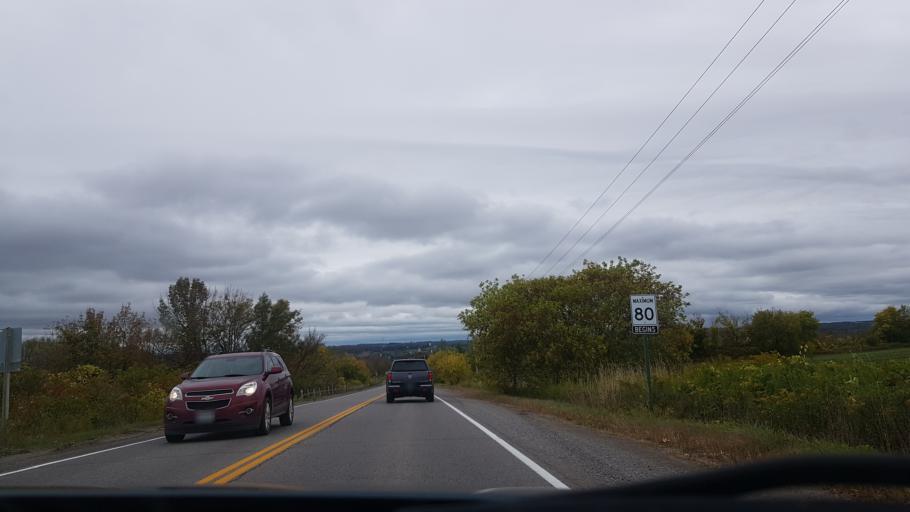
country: CA
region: Ontario
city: Omemee
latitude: 44.2201
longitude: -78.4775
